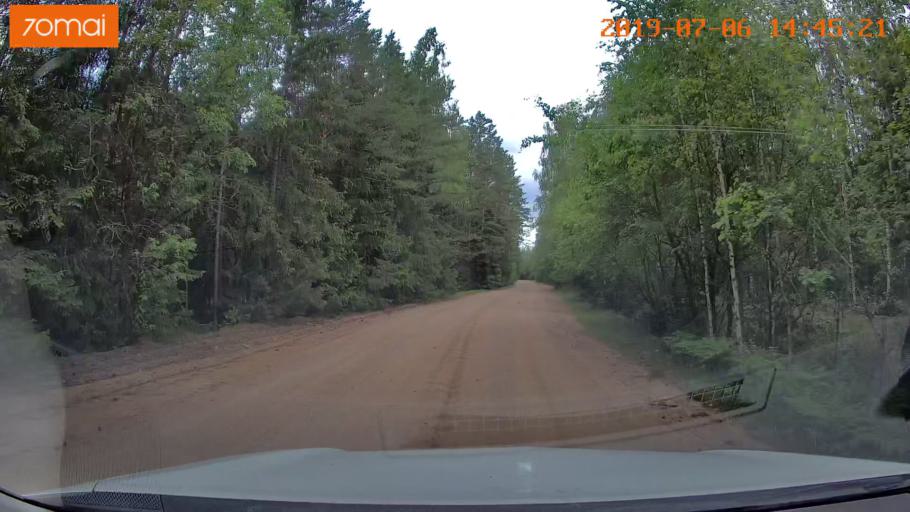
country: BY
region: Minsk
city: Ivyanyets
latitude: 53.9711
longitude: 26.6874
